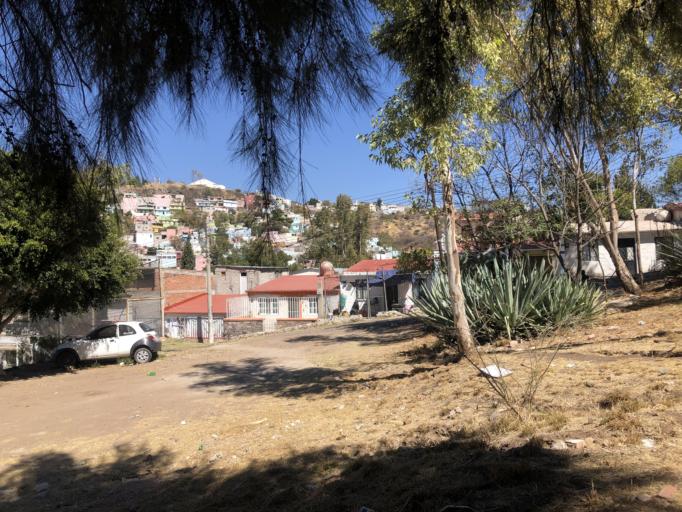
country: MX
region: Queretaro
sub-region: Queretaro
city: Santiago de Queretaro
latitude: 20.6133
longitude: -100.3730
